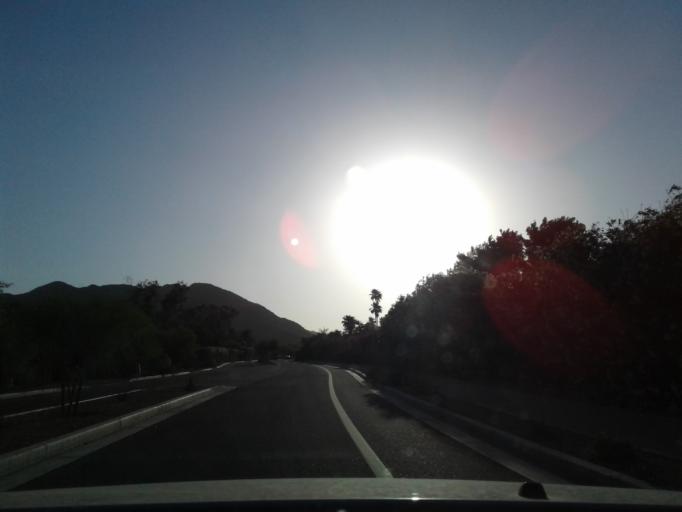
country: US
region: Arizona
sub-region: Maricopa County
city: Paradise Valley
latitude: 33.5609
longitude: -111.9654
